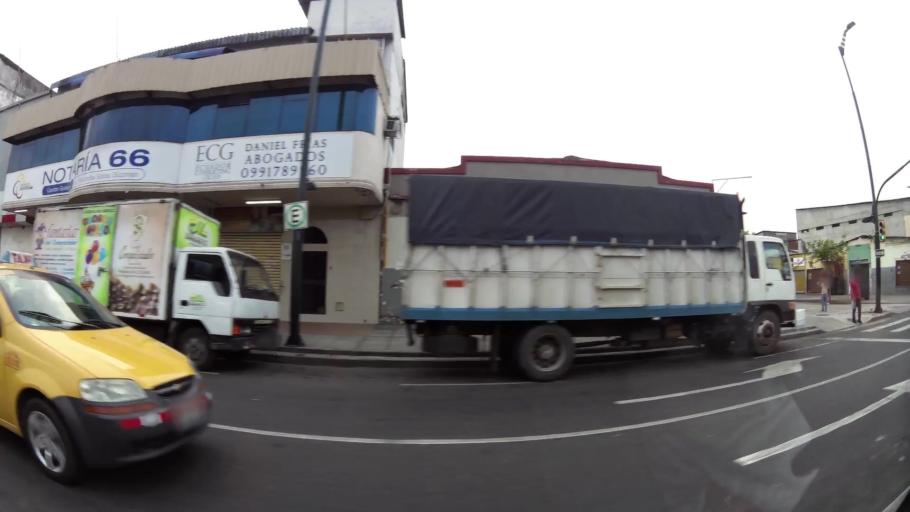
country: EC
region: Guayas
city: Guayaquil
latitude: -2.1978
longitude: -79.8926
